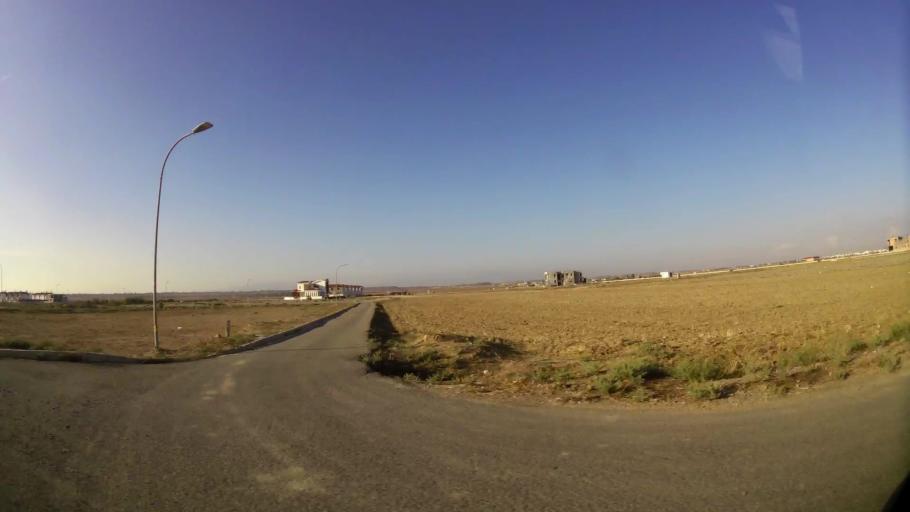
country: CY
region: Lefkosia
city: Nicosia
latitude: 35.2073
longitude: 33.2914
